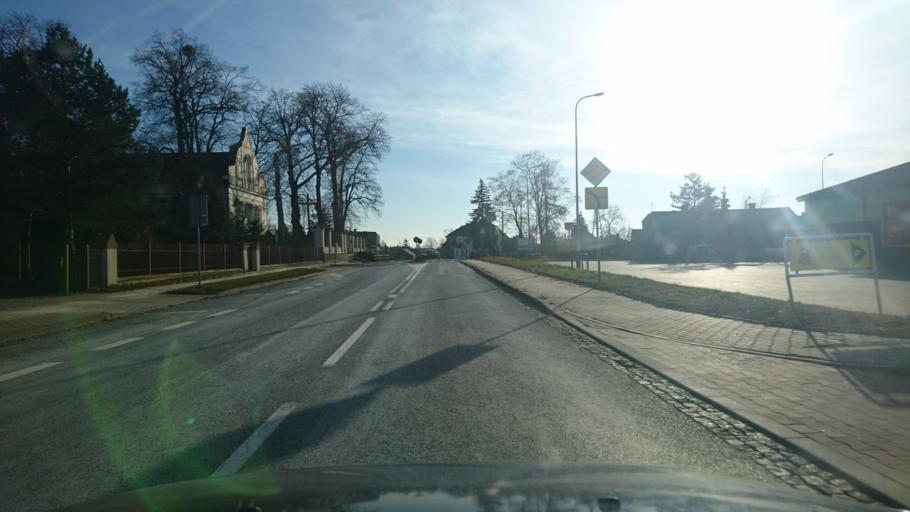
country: PL
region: Opole Voivodeship
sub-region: Powiat oleski
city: Dalachow
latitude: 51.0397
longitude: 18.5979
